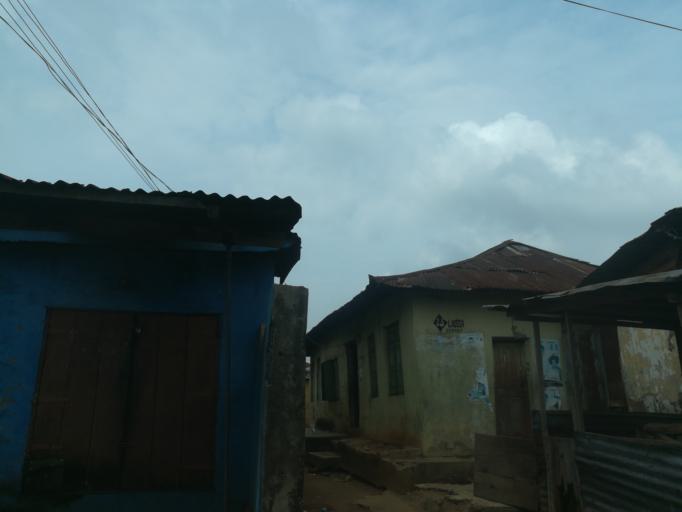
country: NG
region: Lagos
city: Ikorodu
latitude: 6.6148
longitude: 3.5046
